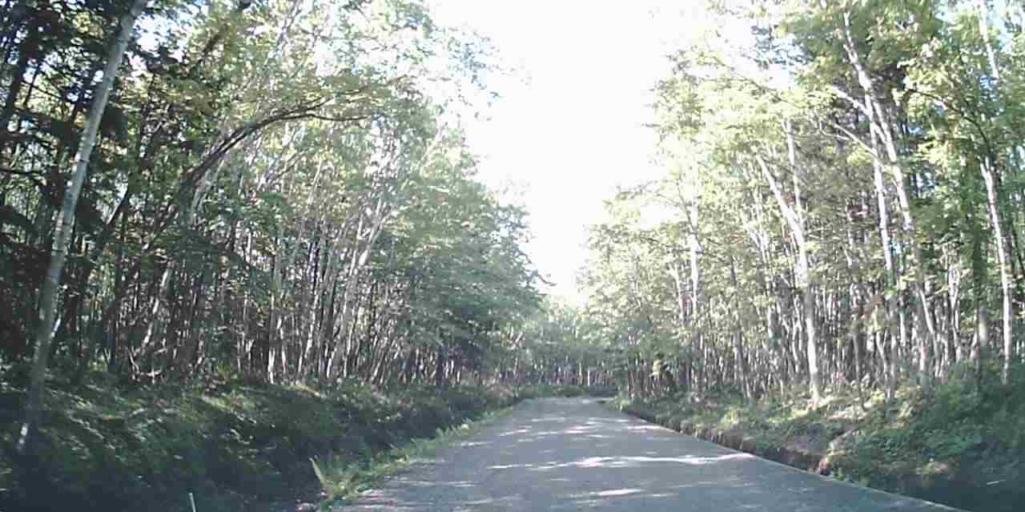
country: JP
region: Hokkaido
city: Shiraoi
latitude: 42.7116
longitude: 141.3998
